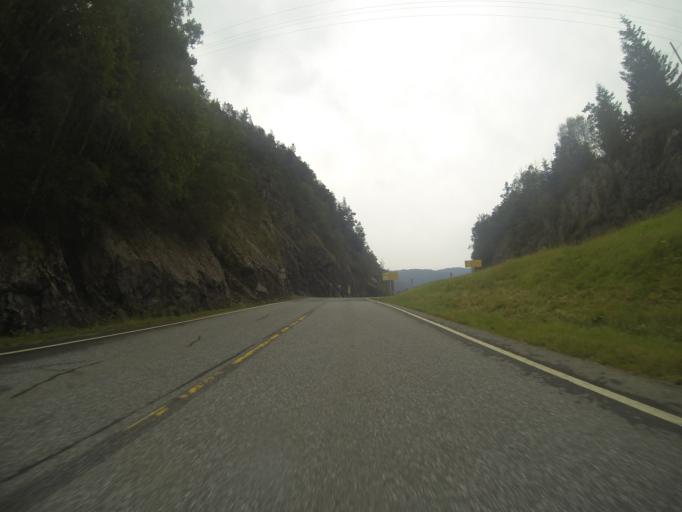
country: NO
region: Rogaland
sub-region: Suldal
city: Sand
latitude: 59.4835
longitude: 6.2010
